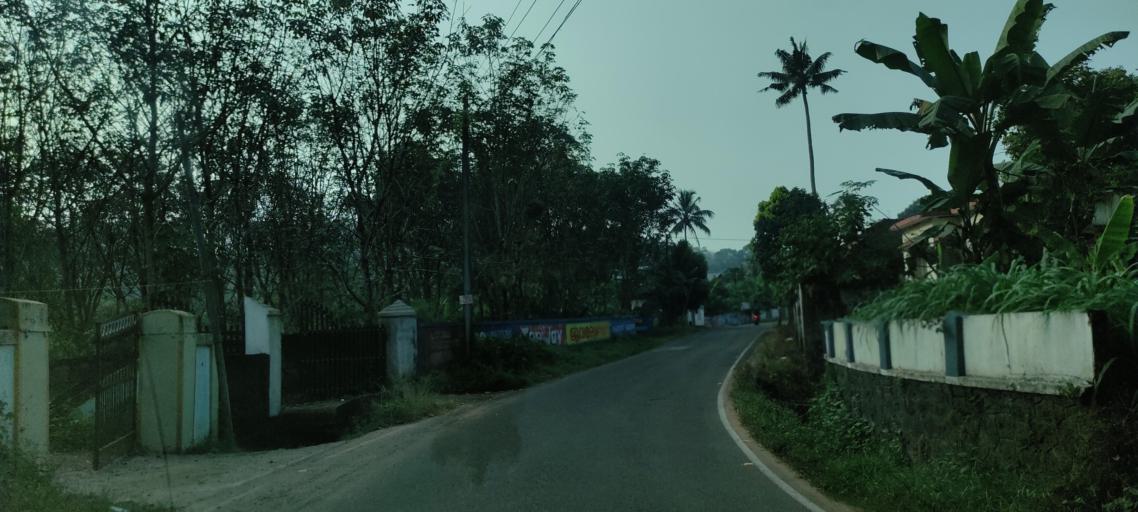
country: IN
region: Kerala
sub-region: Ernakulam
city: Piravam
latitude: 9.8002
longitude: 76.4999
